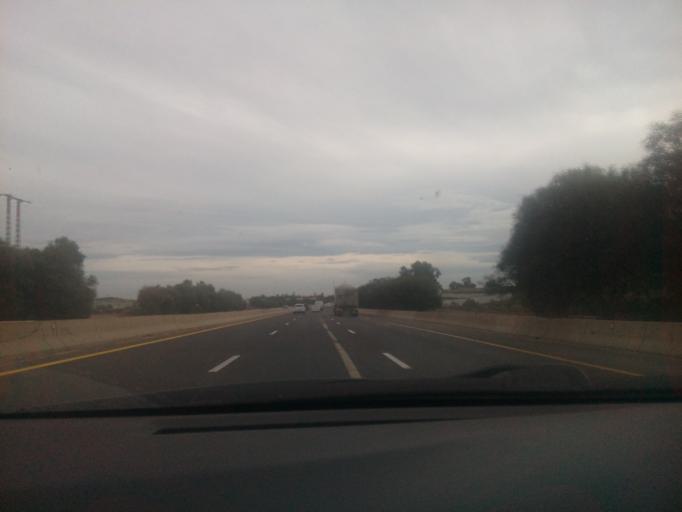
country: DZ
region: Oran
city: Sidi ech Chahmi
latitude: 35.5728
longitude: -0.5459
